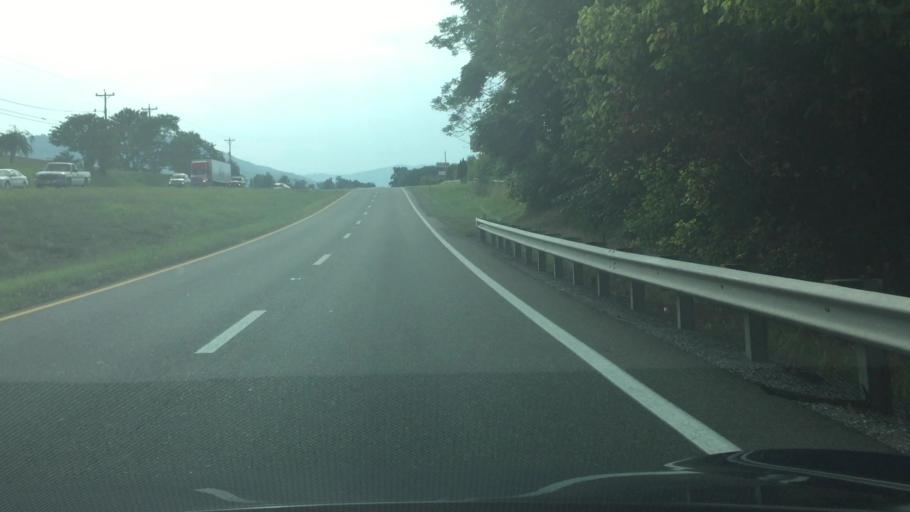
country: US
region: Virginia
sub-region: City of Bedford
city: Bedford
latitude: 37.3563
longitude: -79.6599
